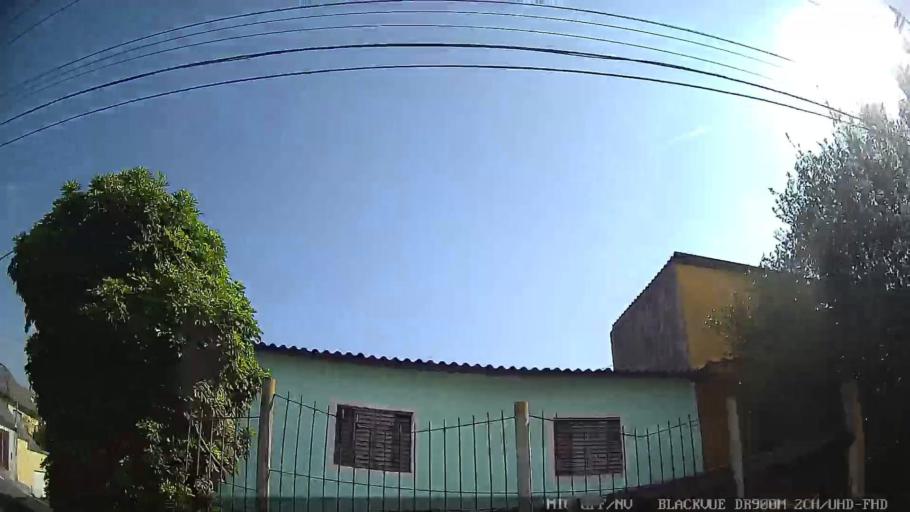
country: BR
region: Sao Paulo
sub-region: Ferraz De Vasconcelos
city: Ferraz de Vasconcelos
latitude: -23.5162
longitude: -46.4362
